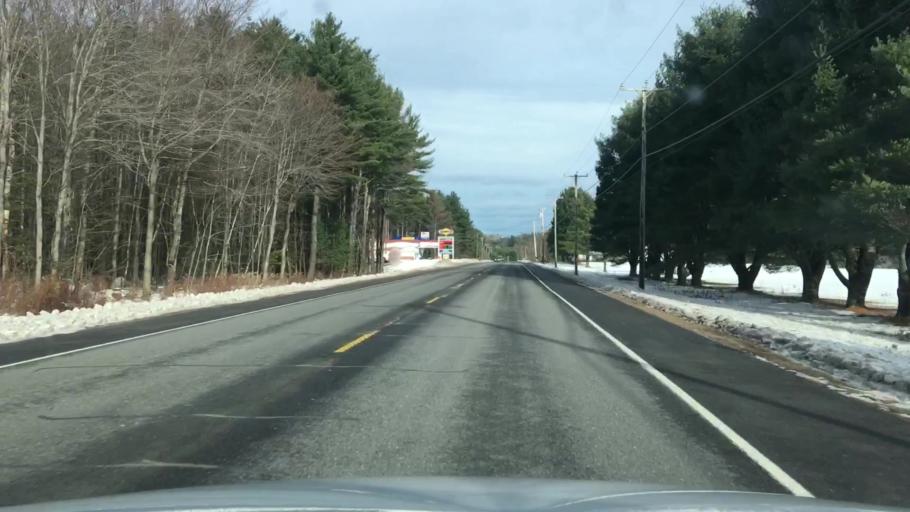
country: US
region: Maine
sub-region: Kennebec County
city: Monmouth
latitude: 44.2213
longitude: -70.0902
